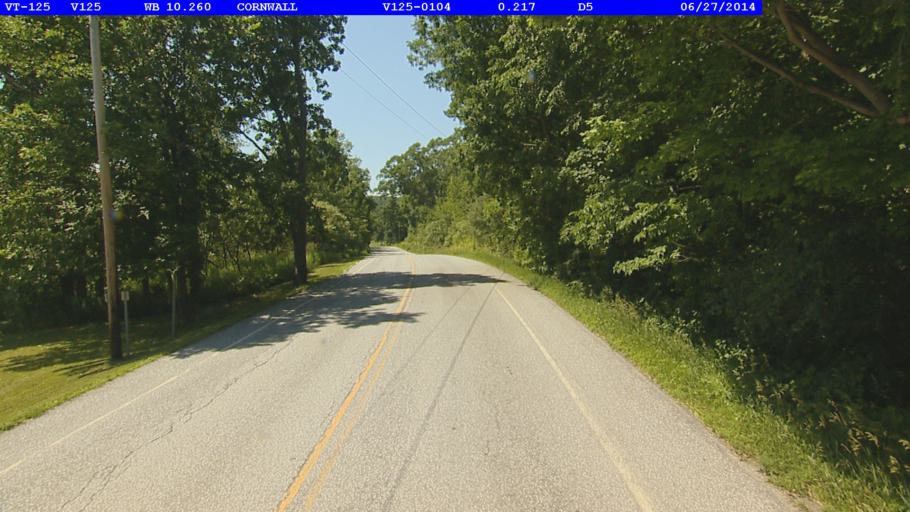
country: US
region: Vermont
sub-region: Addison County
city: Middlebury (village)
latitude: 43.9948
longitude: -73.2538
